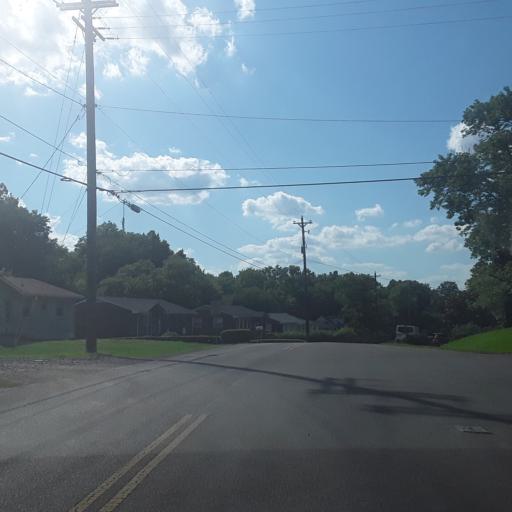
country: US
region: Tennessee
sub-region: Davidson County
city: Lakewood
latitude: 36.2038
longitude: -86.6362
